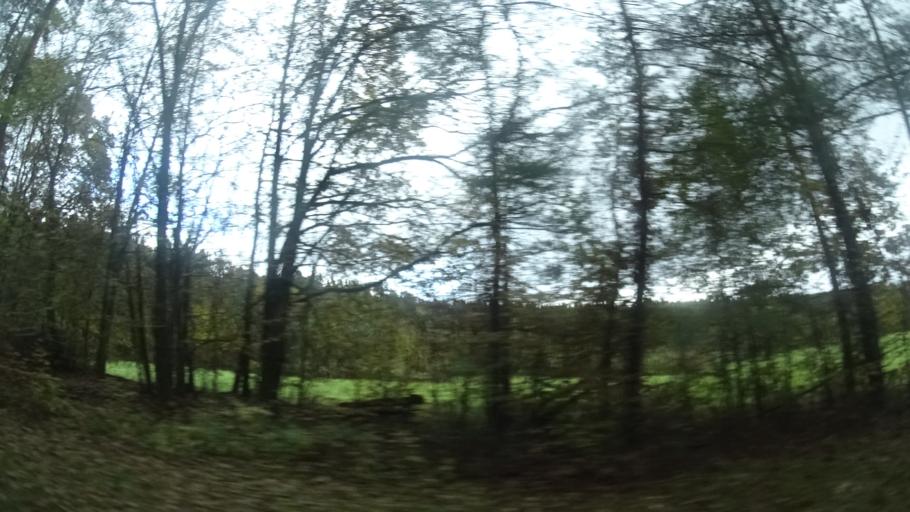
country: DE
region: Bavaria
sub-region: Regierungsbezirk Unterfranken
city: Oberelsbach
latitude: 50.3591
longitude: 10.1004
